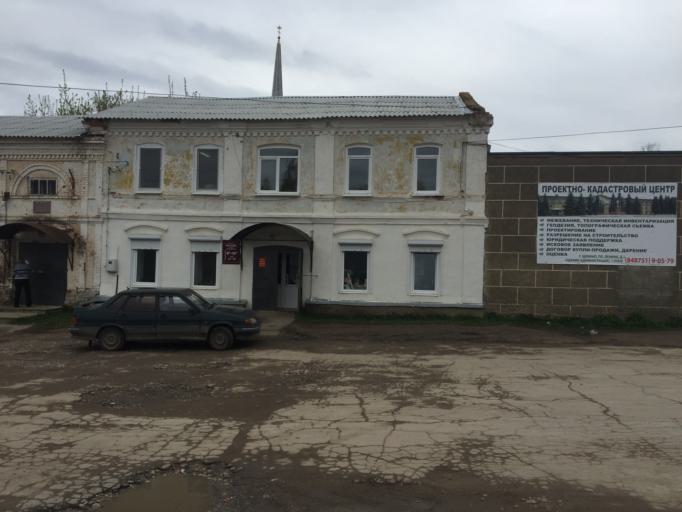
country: RU
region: Tula
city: Krapivna
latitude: 53.9412
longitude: 37.1540
